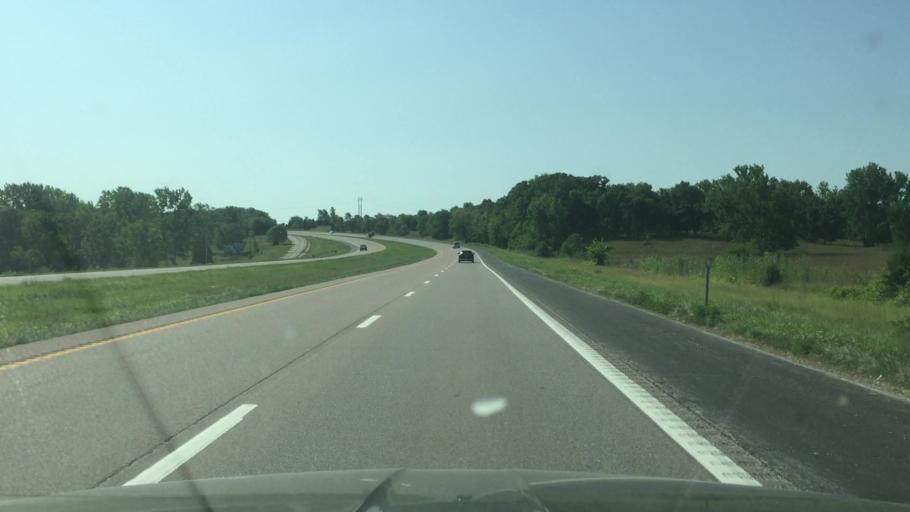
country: US
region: Missouri
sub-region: Pettis County
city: Sedalia
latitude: 38.7241
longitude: -93.3021
